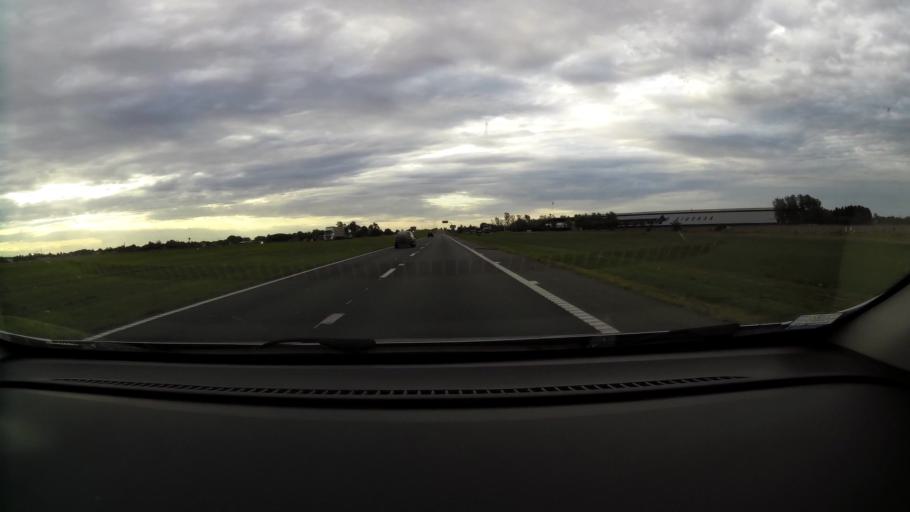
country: AR
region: Buenos Aires
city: San Nicolas de los Arroyos
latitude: -33.3933
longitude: -60.2146
